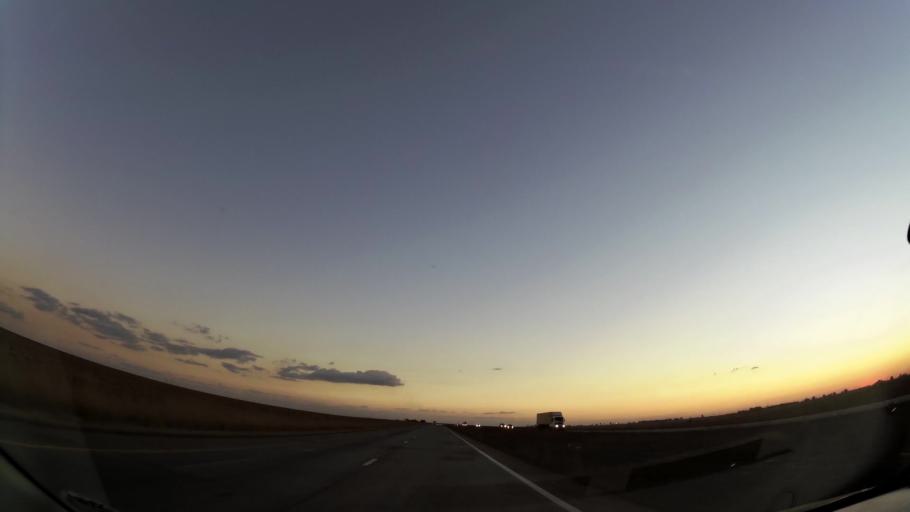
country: ZA
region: Mpumalanga
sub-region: Nkangala District Municipality
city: Witbank
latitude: -25.9825
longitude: 29.1633
